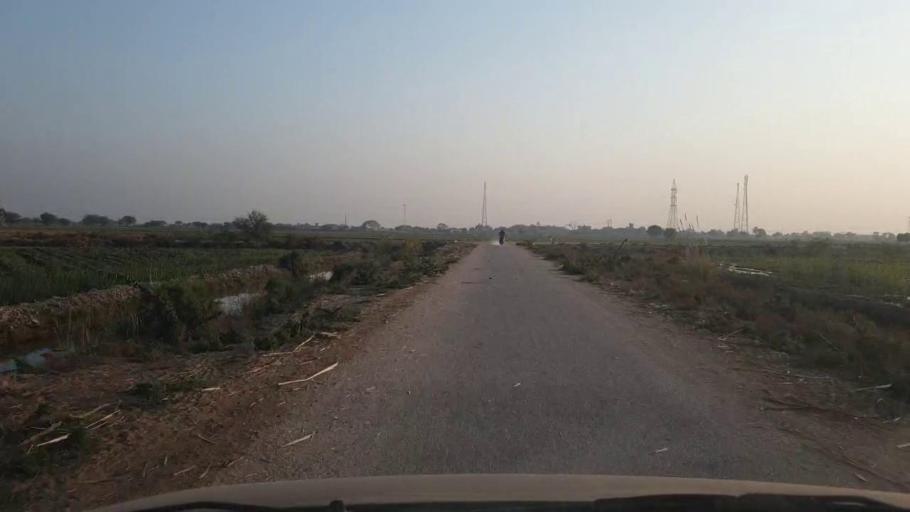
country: PK
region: Sindh
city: Mirwah Gorchani
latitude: 25.3206
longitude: 69.1573
